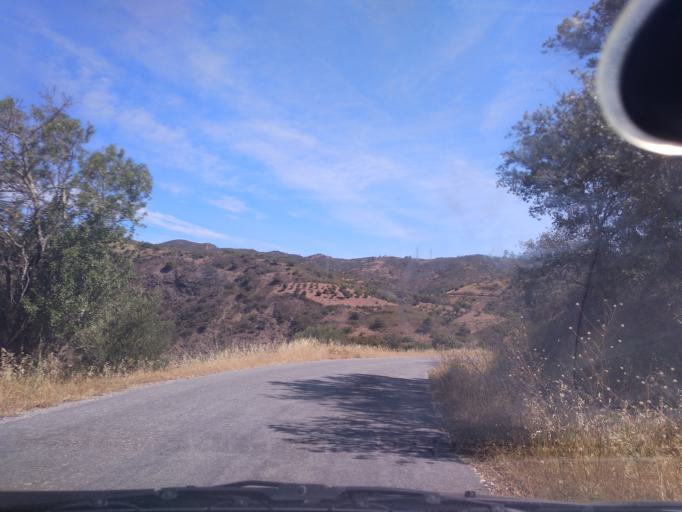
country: PT
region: Faro
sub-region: Sao Bras de Alportel
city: Sao Bras de Alportel
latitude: 37.1770
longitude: -7.8075
